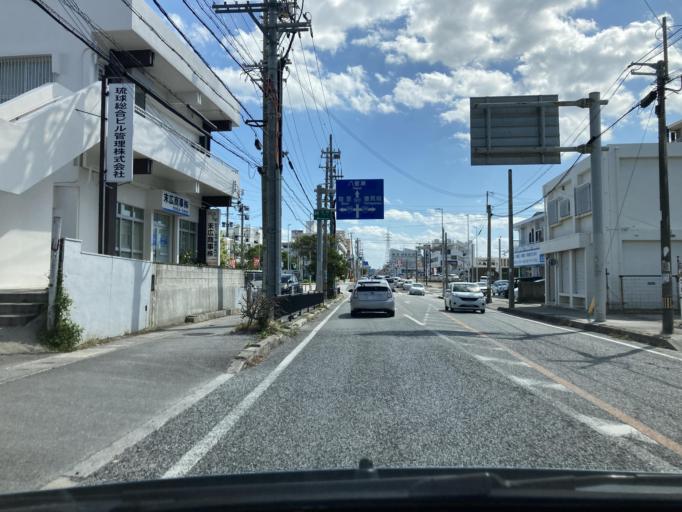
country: JP
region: Okinawa
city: Tomigusuku
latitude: 26.1933
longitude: 127.7066
